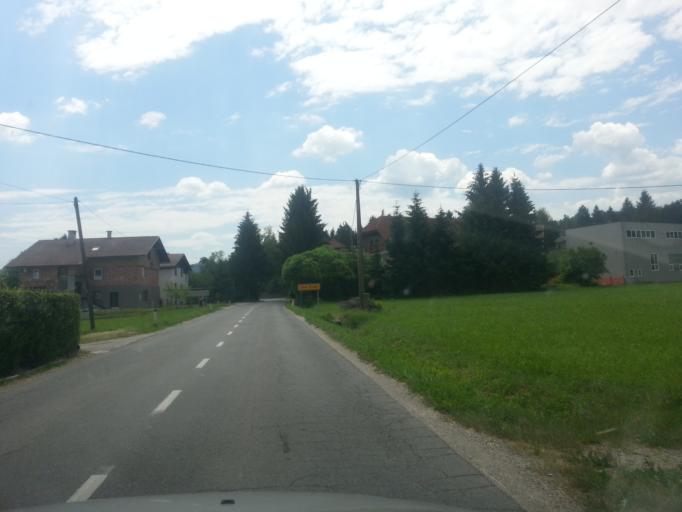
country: SI
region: Vrhnika
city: Vrhnika
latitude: 45.9756
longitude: 14.2909
